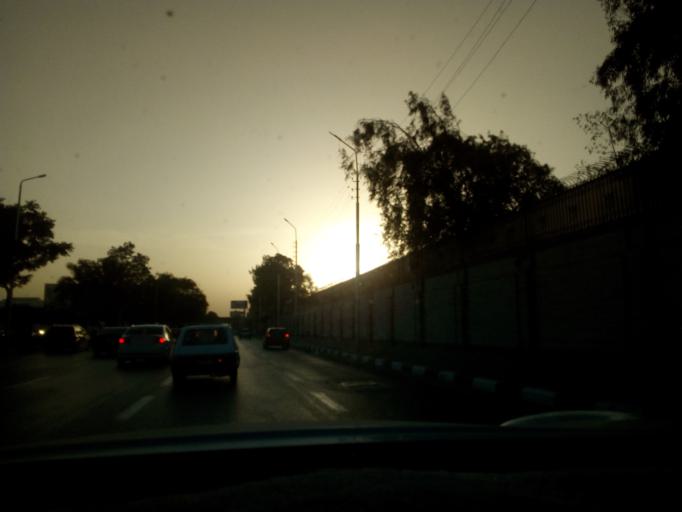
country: EG
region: Muhafazat al Qalyubiyah
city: Al Khankah
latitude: 30.1021
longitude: 31.3537
